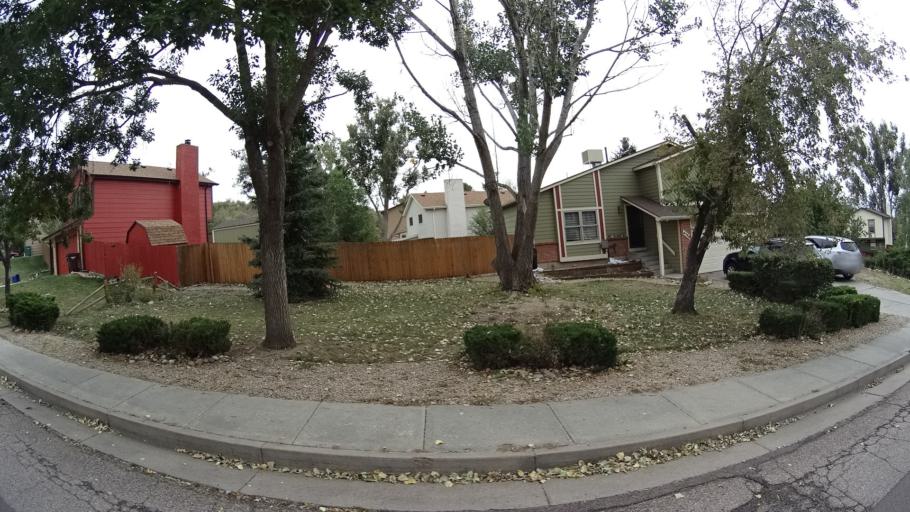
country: US
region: Colorado
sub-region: El Paso County
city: Cimarron Hills
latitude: 38.9078
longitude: -104.7316
